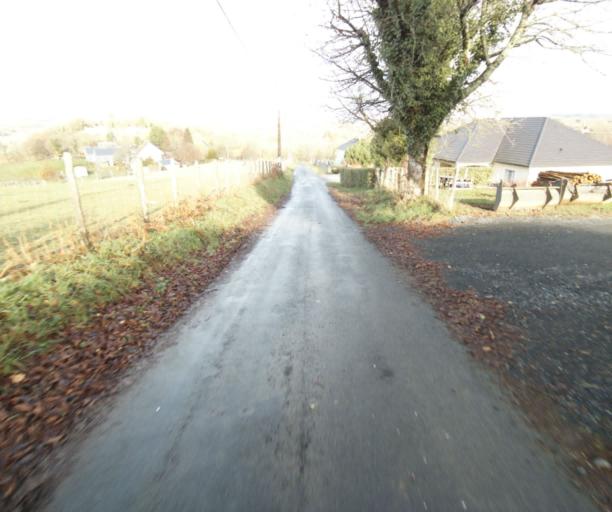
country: FR
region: Limousin
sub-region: Departement de la Correze
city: Sainte-Fereole
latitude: 45.2480
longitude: 1.6090
